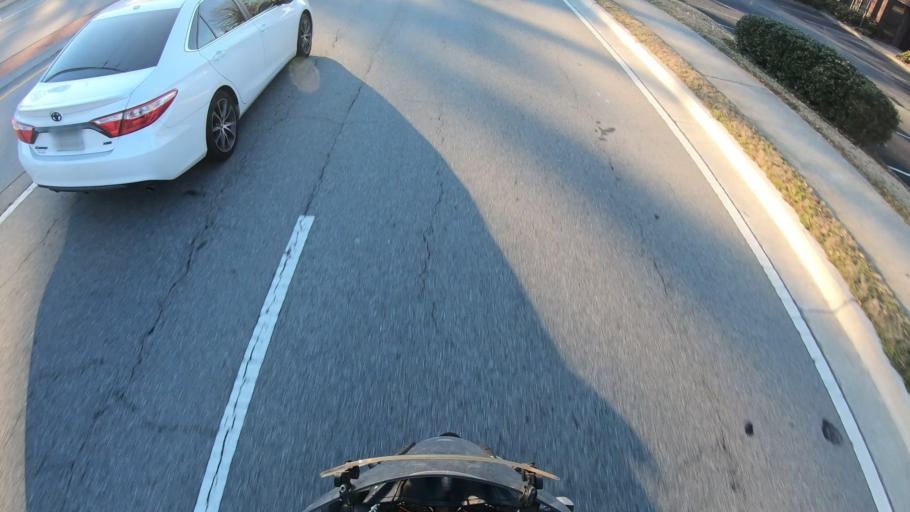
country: US
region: Georgia
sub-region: Cobb County
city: Kennesaw
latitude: 34.0475
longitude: -84.6066
